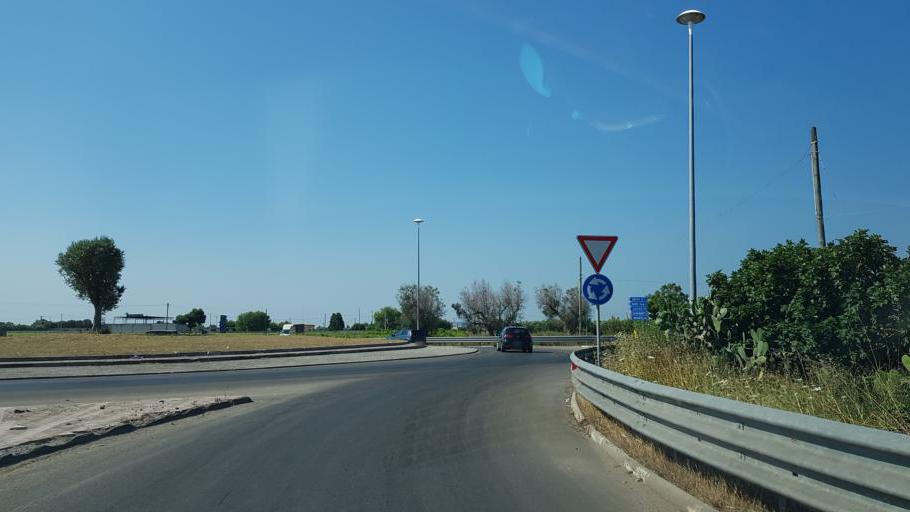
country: IT
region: Apulia
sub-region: Provincia di Lecce
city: Salice Salentino
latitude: 40.4010
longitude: 17.9710
